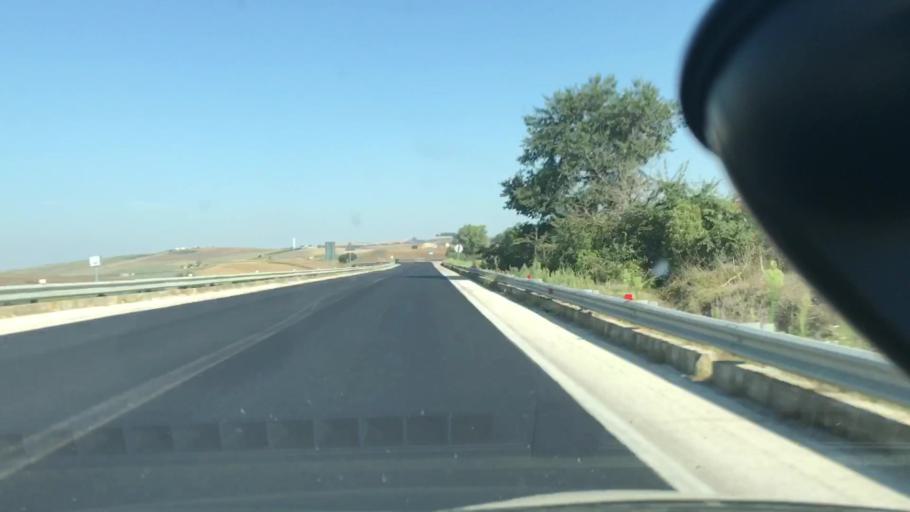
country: IT
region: Apulia
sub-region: Provincia di Barletta - Andria - Trani
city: Spinazzola
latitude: 40.9100
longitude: 16.1069
